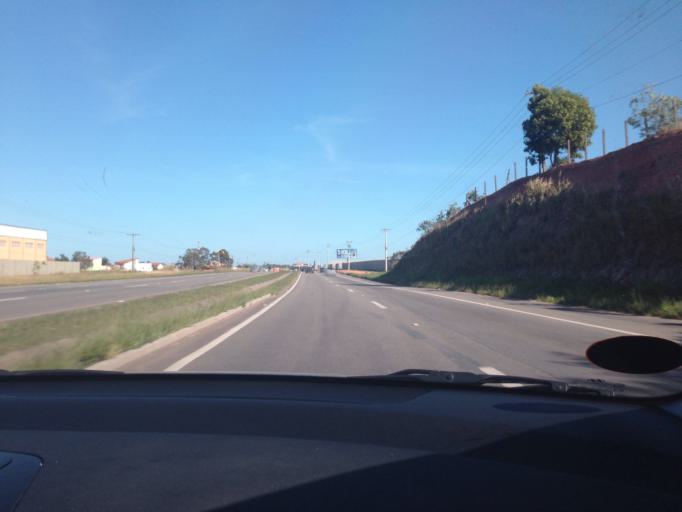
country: BR
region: Espirito Santo
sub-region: Vitoria
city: Vitoria
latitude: -20.4748
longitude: -40.3527
